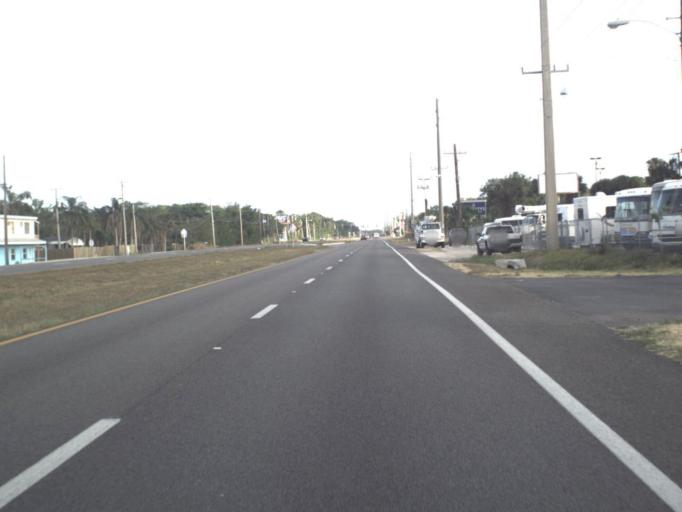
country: US
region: Florida
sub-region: Brevard County
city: Sharpes
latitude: 28.4361
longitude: -80.7614
